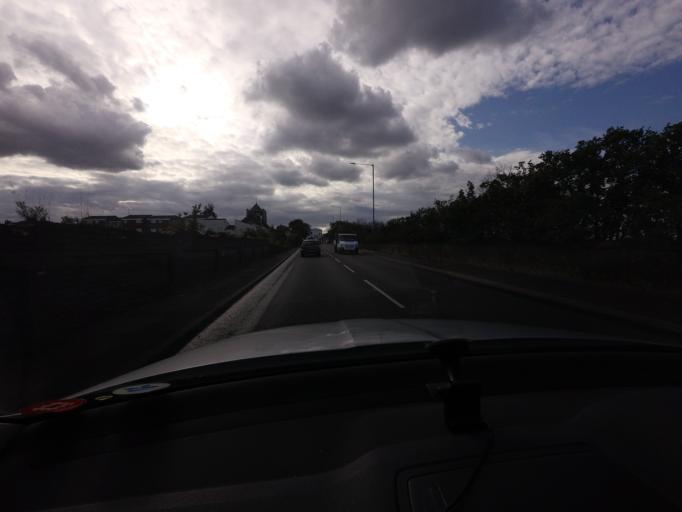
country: GB
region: England
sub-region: Kent
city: Swanscombe
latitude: 51.4501
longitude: 0.3112
